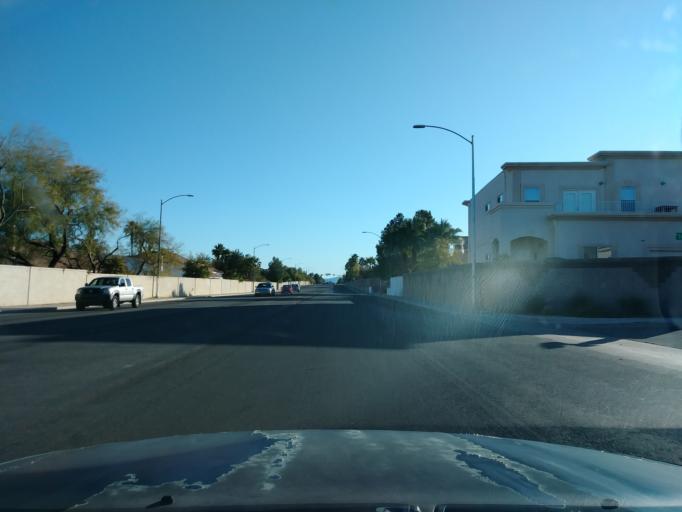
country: US
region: Nevada
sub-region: Clark County
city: Spring Valley
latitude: 36.1548
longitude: -115.2710
